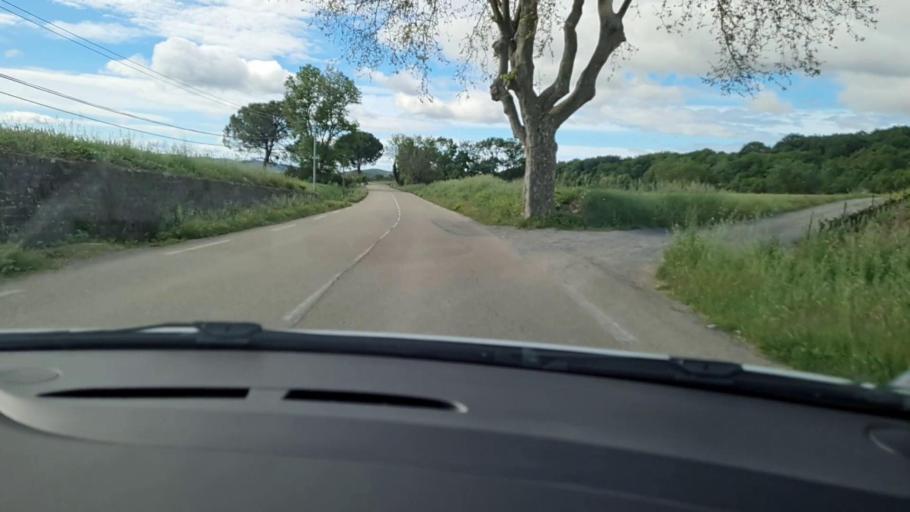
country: FR
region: Languedoc-Roussillon
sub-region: Departement du Gard
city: Quissac
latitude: 43.9002
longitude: 4.0012
